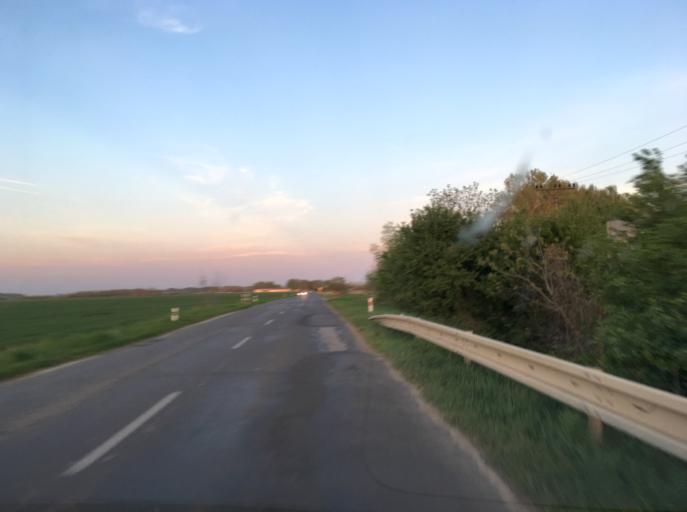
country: SK
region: Nitriansky
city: Kolarovo
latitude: 47.9252
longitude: 18.0216
